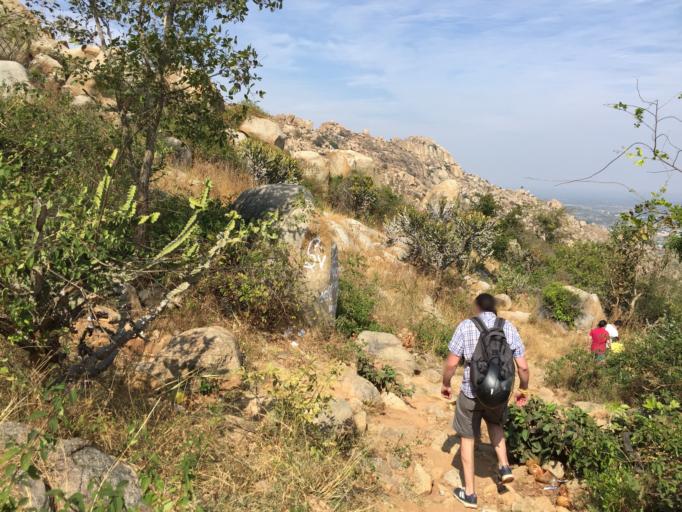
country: IN
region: Karnataka
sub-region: Kolar
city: Kolar
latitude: 13.1404
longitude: 78.0965
